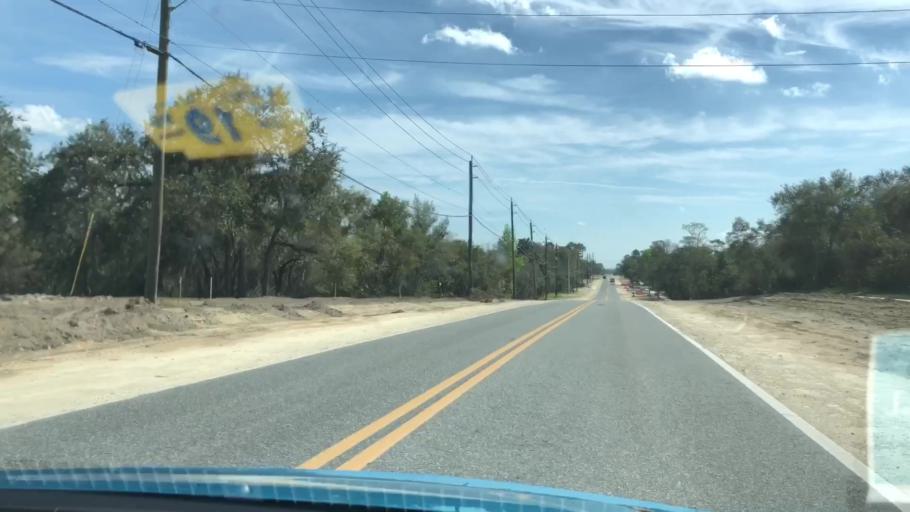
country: US
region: Florida
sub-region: Seminole County
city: Midway
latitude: 28.8587
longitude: -81.1941
